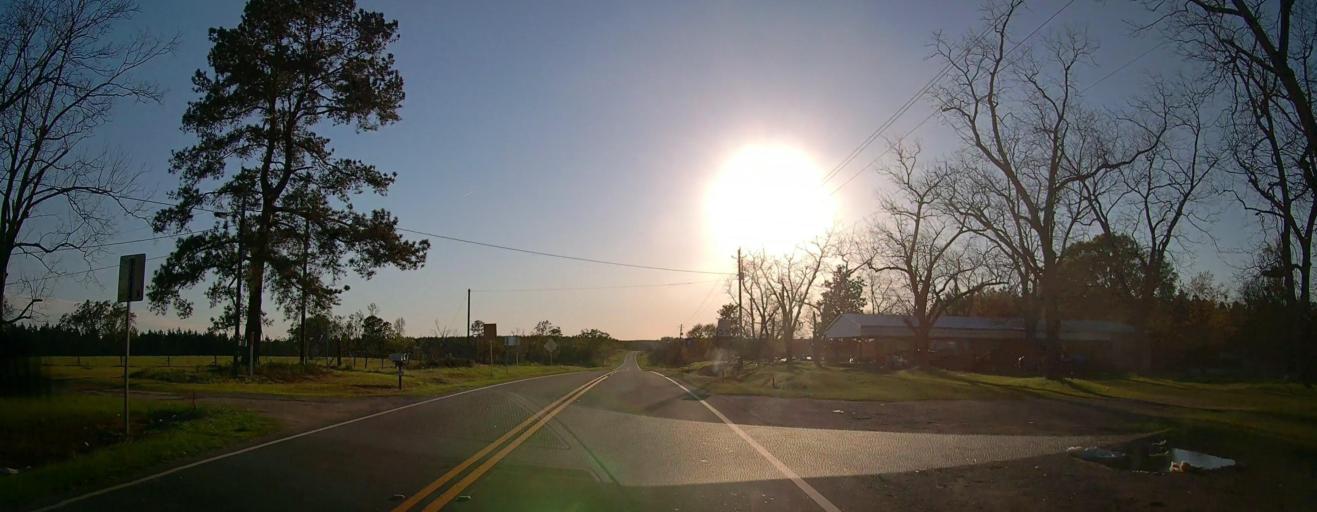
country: US
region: Georgia
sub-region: Wilcox County
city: Abbeville
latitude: 31.9909
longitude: -83.3230
